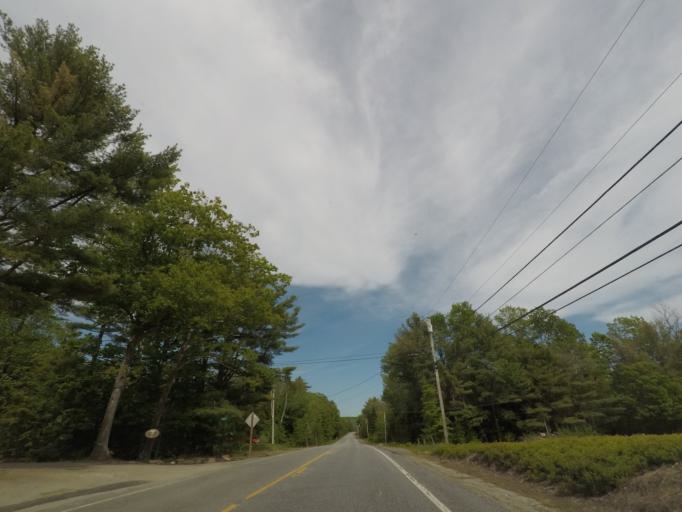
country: US
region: Maine
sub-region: Sagadahoc County
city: Richmond
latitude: 44.0872
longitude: -69.7682
